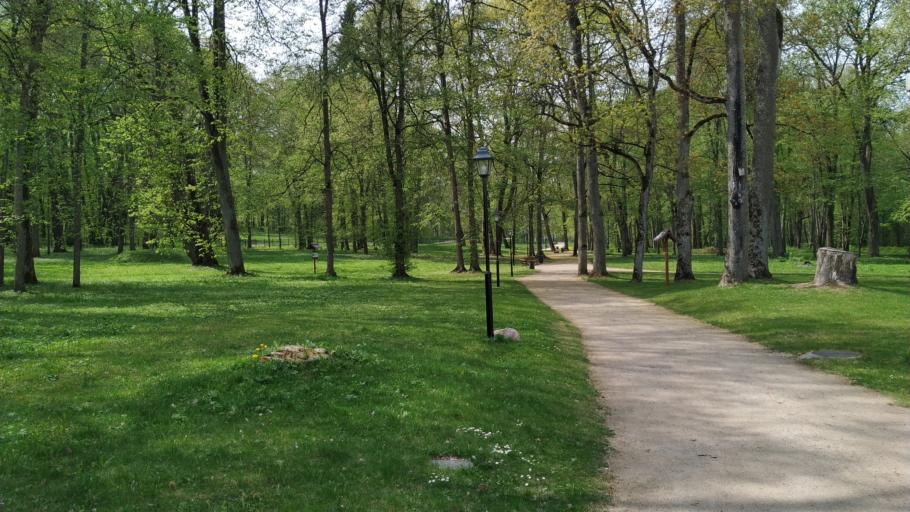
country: LT
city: Salcininkai
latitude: 54.4334
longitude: 25.2982
